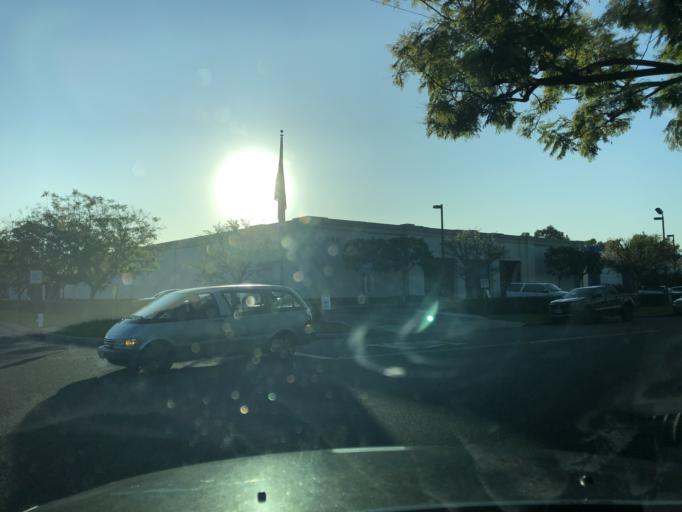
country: US
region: California
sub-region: Orange County
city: Irvine
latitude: 33.6743
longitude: -117.8752
